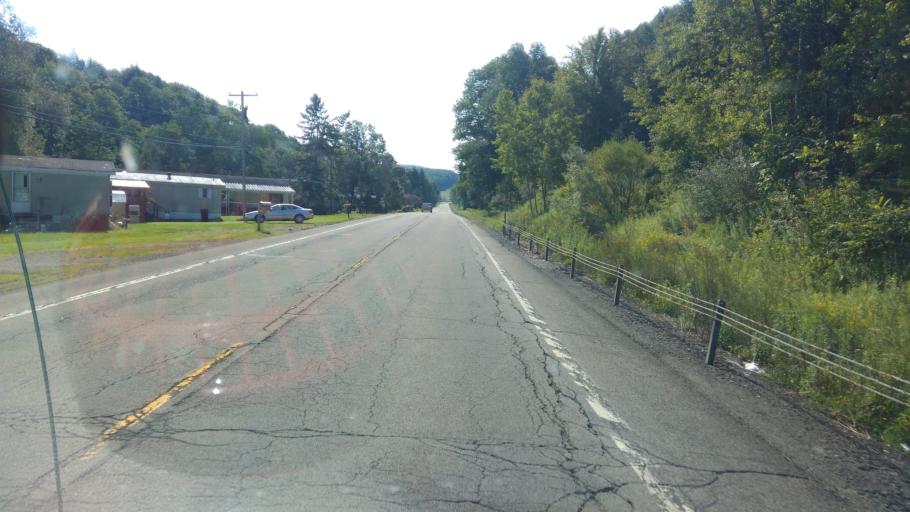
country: US
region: New York
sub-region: Allegany County
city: Cuba
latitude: 42.1895
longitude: -78.2646
